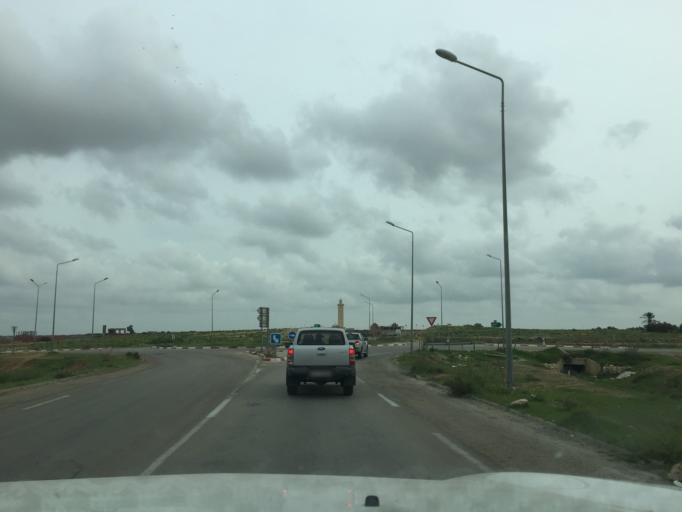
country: TN
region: Susah
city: Masakin
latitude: 35.6469
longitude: 10.5858
